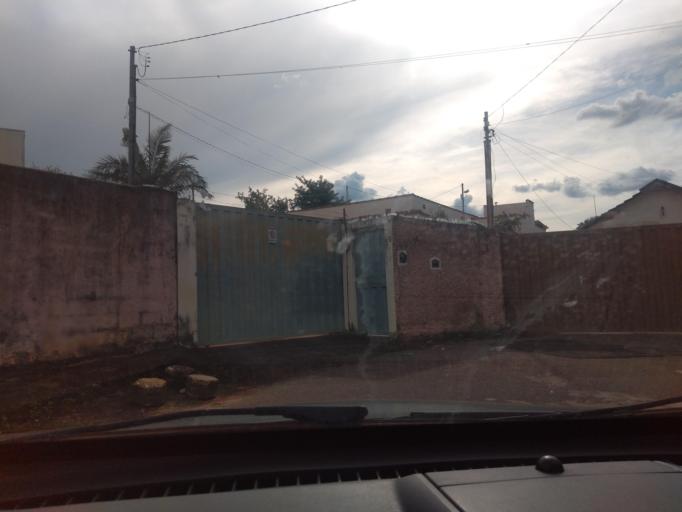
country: BR
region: Minas Gerais
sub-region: Tres Coracoes
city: Tres Coracoes
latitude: -21.7124
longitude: -45.2644
